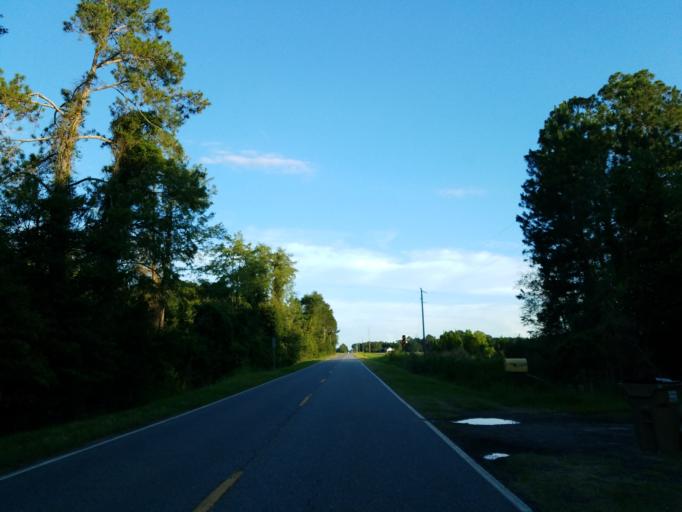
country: US
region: Georgia
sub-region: Tift County
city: Unionville
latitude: 31.3230
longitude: -83.4774
